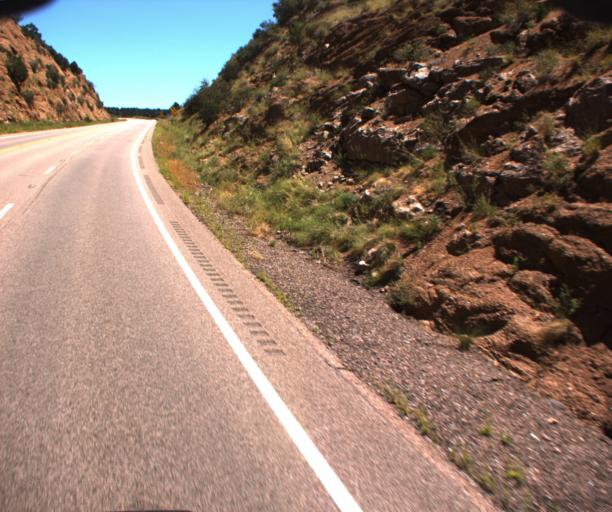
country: US
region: Arizona
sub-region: Gila County
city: San Carlos
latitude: 33.6500
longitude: -110.5742
